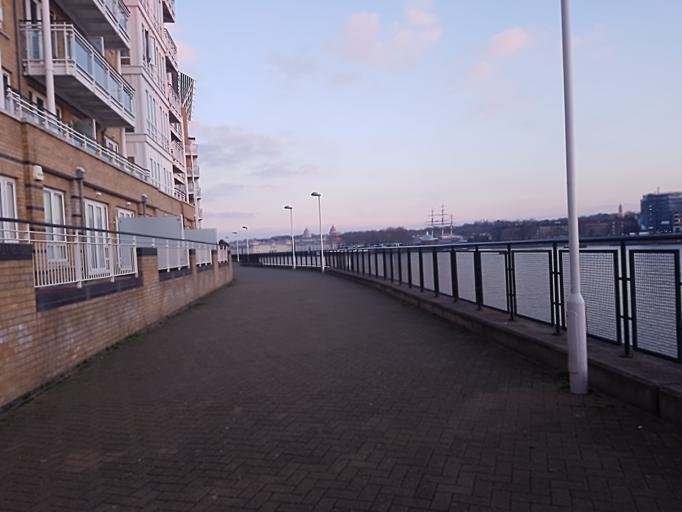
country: GB
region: England
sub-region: Greater London
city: Poplar
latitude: 51.4863
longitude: -0.0170
